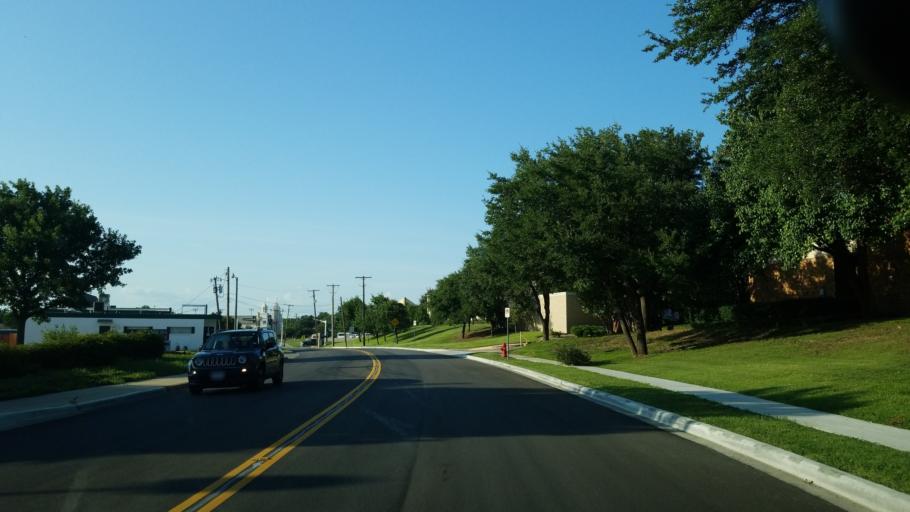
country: US
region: Texas
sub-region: Dallas County
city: Farmers Branch
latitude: 32.9367
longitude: -96.8852
